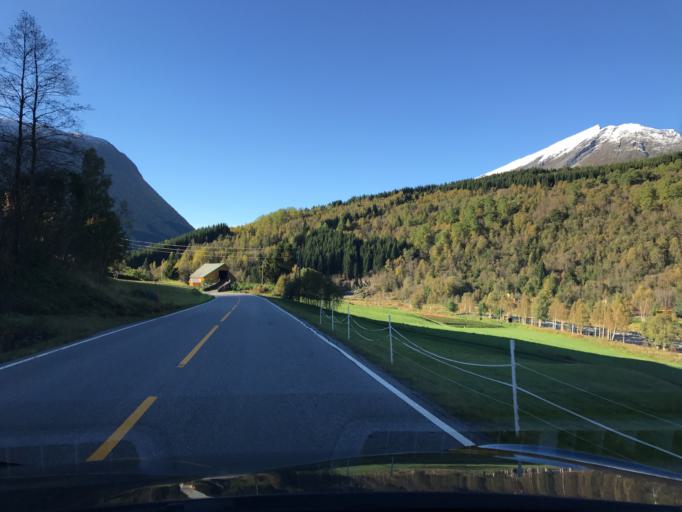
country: NO
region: More og Romsdal
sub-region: Norddal
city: Valldal
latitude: 62.3404
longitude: 7.3960
